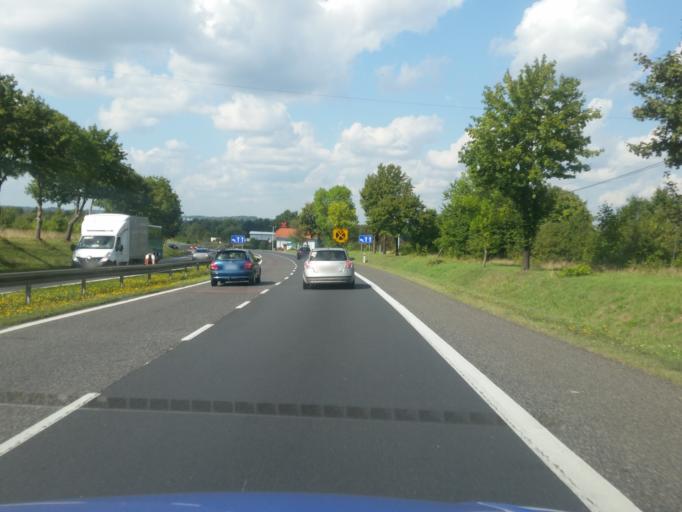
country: PL
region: Silesian Voivodeship
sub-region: Powiat myszkowski
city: Kozieglowy
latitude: 50.5891
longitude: 19.1611
